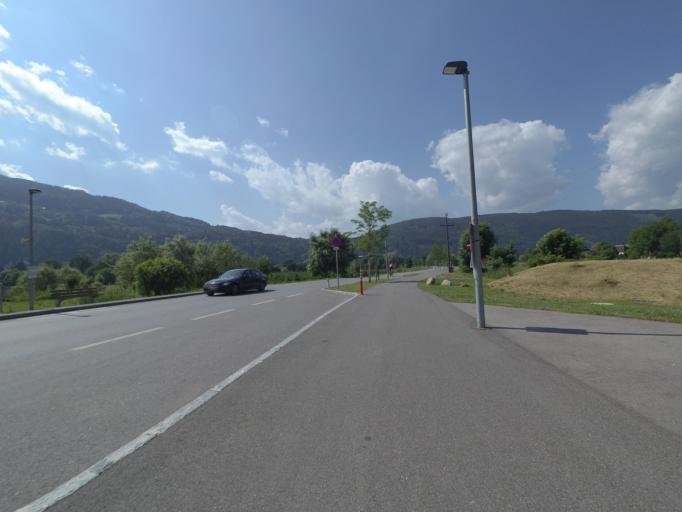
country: AT
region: Carinthia
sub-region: Politischer Bezirk Villach Land
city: Ferndorf
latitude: 46.7797
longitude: 13.6452
